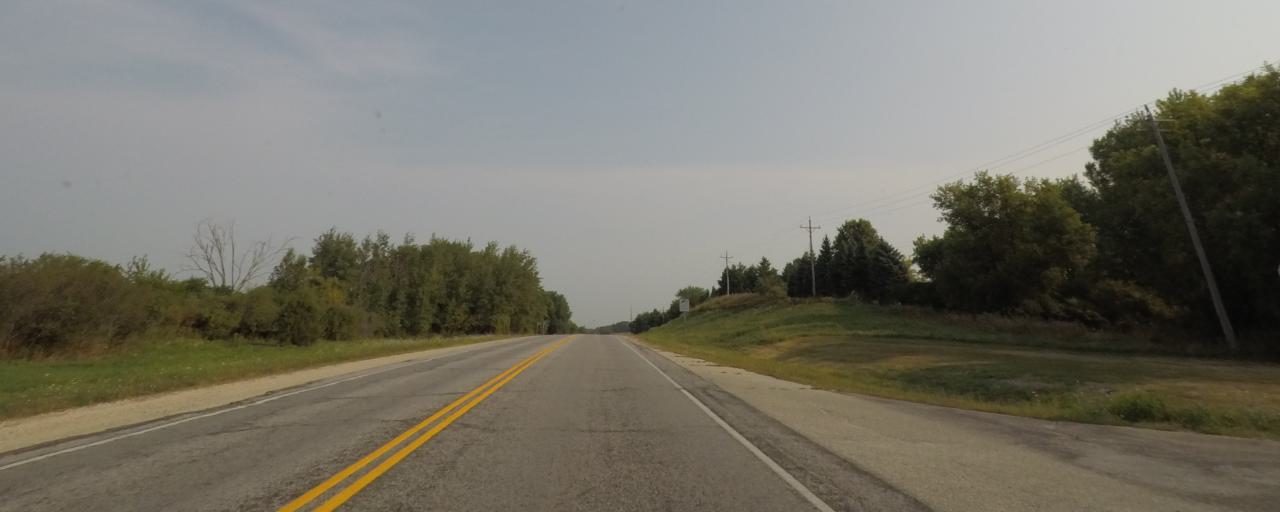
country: US
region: Wisconsin
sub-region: Dane County
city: Deerfield
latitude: 43.0918
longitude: -89.0802
